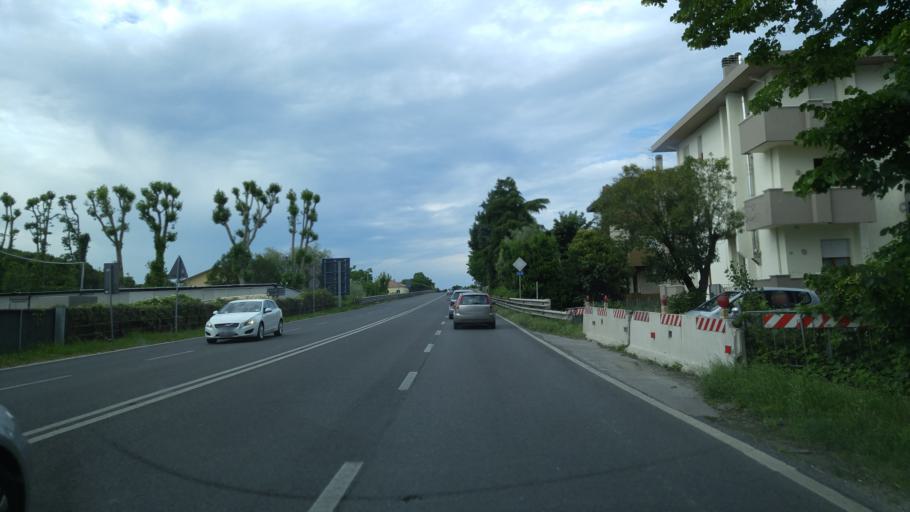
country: IT
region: Emilia-Romagna
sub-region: Provincia di Rimini
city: Rimini
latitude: 44.0660
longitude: 12.5415
